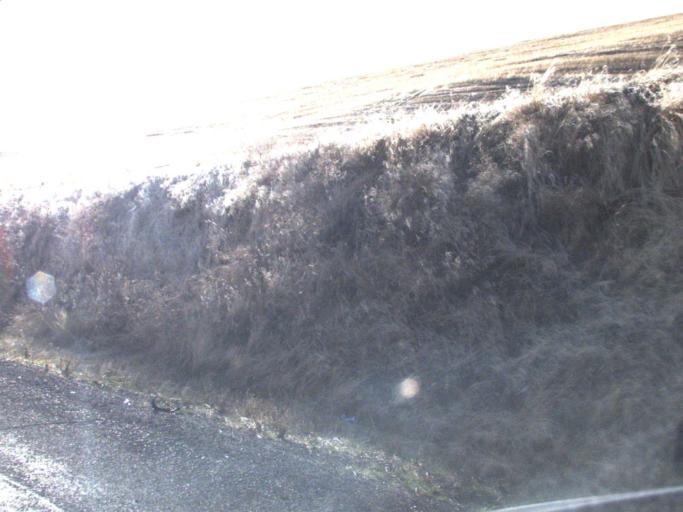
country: US
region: Washington
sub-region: Columbia County
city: Dayton
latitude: 46.3694
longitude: -117.9463
